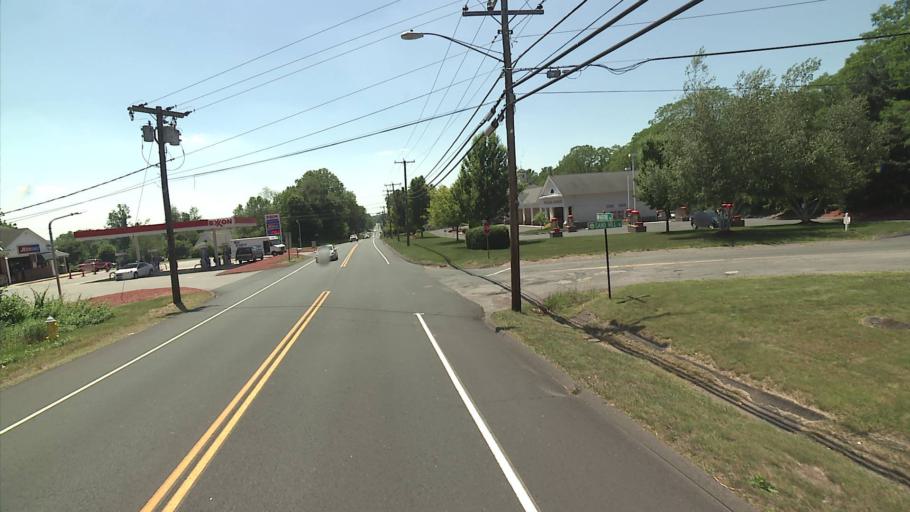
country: US
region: Connecticut
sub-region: Tolland County
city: Rockville
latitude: 41.8662
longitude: -72.4176
